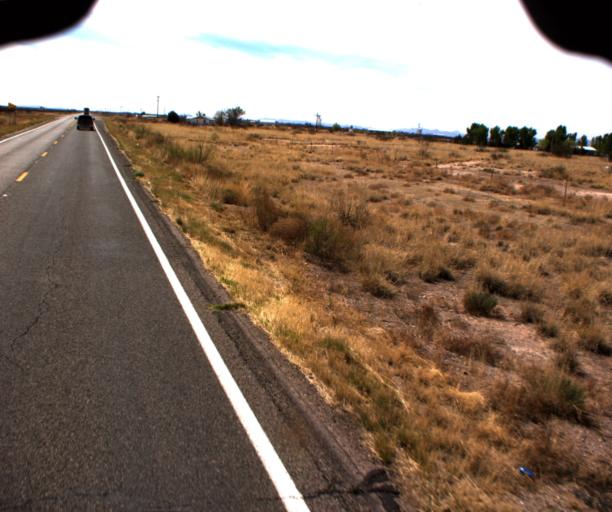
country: US
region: Arizona
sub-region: Cochise County
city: Bisbee
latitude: 31.6731
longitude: -109.6838
